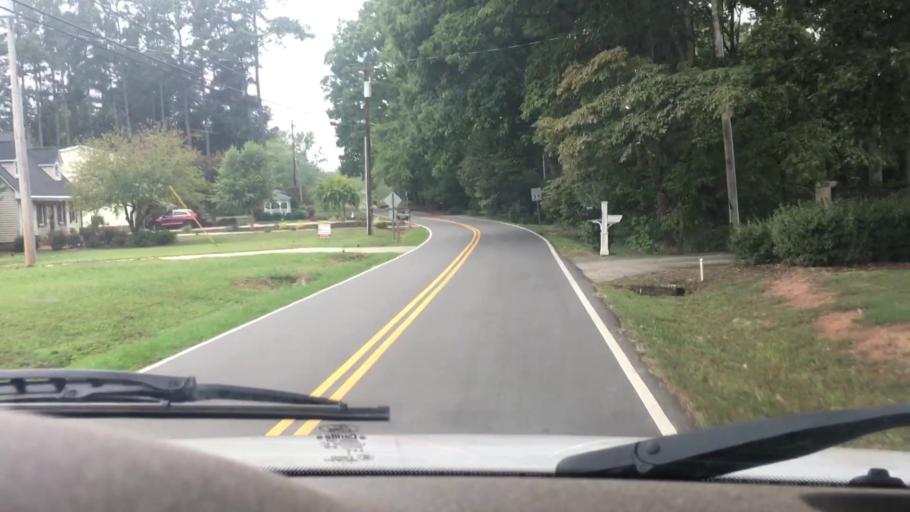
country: US
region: North Carolina
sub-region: Mecklenburg County
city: Cornelius
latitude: 35.4465
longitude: -80.8979
